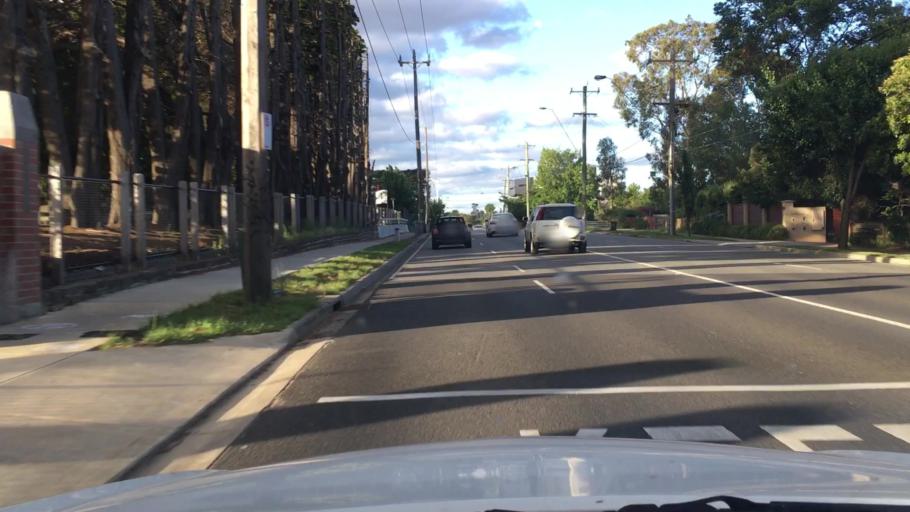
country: AU
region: Victoria
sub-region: Whitehorse
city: Box Hill
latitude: -37.8224
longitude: 145.1378
